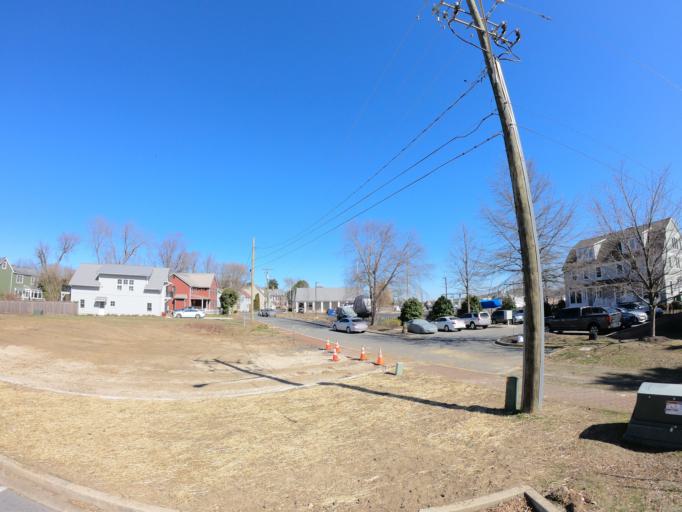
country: US
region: Maryland
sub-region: Kent County
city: Chestertown
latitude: 39.2054
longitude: -76.0659
